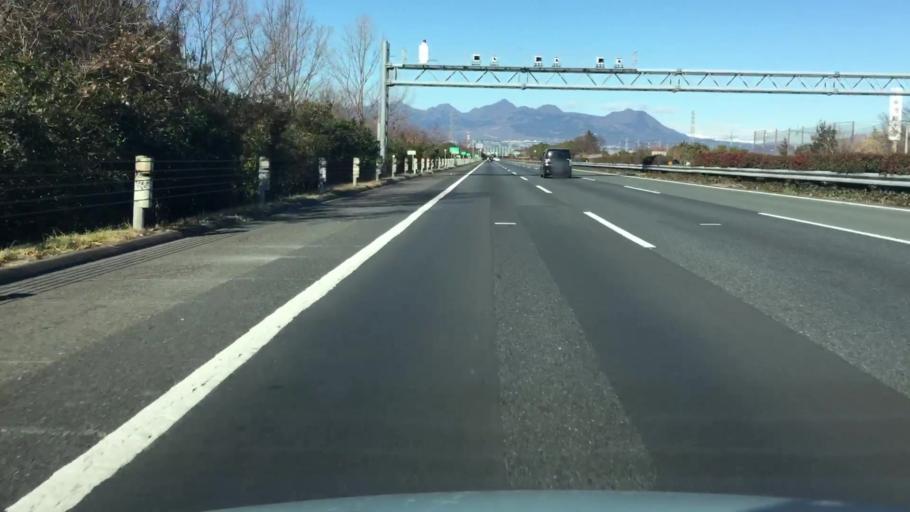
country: JP
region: Gunma
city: Takasaki
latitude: 36.3480
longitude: 139.0497
